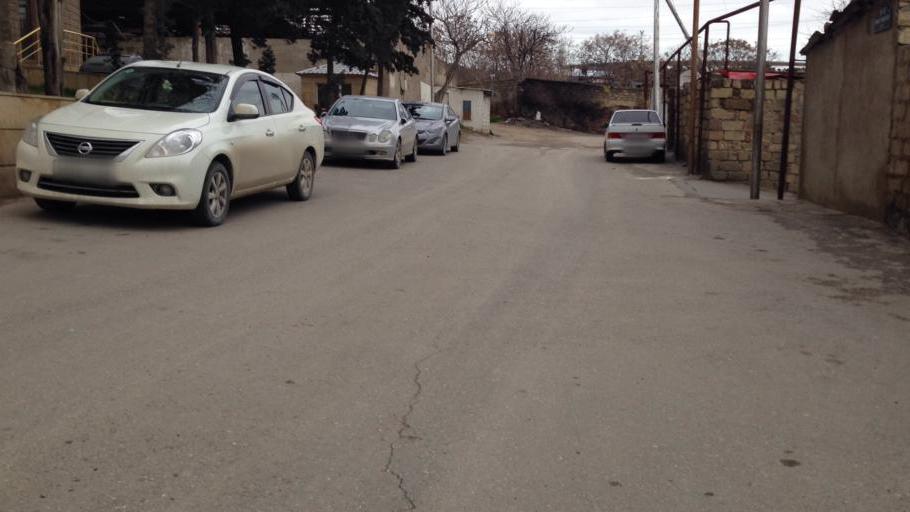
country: AZ
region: Baki
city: Baku
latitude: 40.3927
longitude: 49.8526
